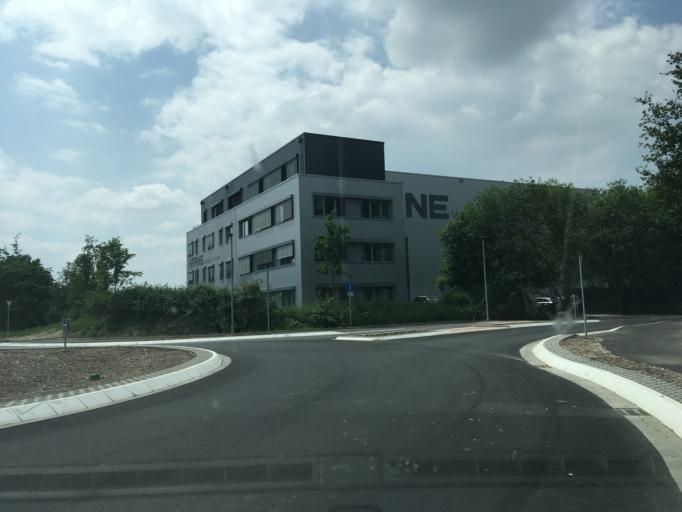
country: DE
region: North Rhine-Westphalia
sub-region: Regierungsbezirk Munster
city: Sudlohn
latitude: 51.9125
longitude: 6.8688
